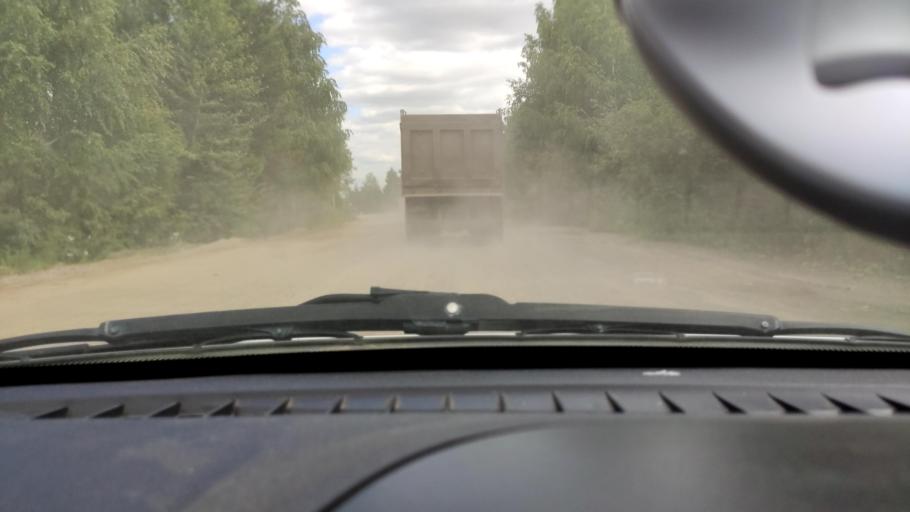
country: RU
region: Perm
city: Kondratovo
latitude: 58.0232
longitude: 56.0733
